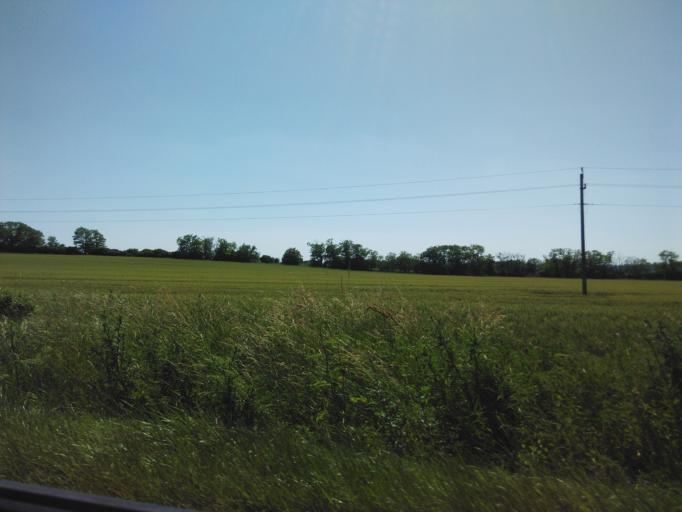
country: HU
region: Fejer
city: Fehervarcsurgo
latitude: 47.3116
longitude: 18.2875
